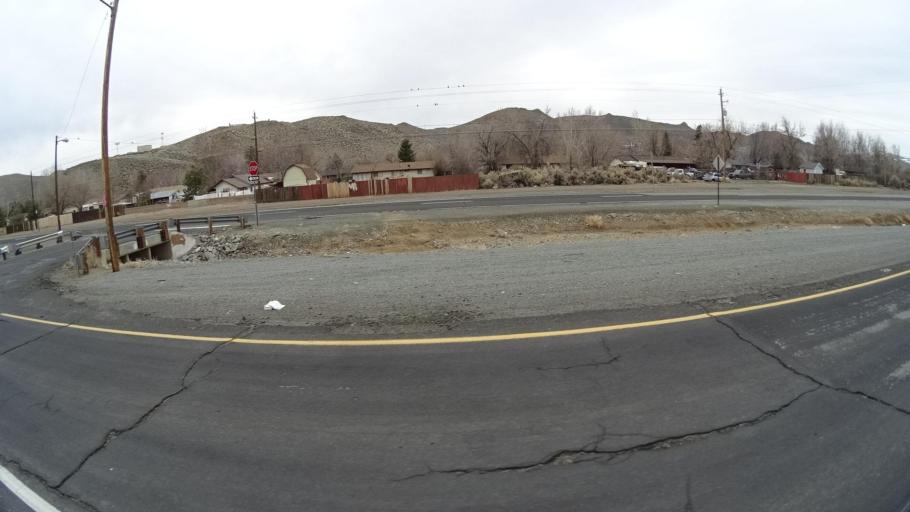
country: US
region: Nevada
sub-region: Washoe County
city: Lemmon Valley
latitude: 39.6396
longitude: -119.8411
